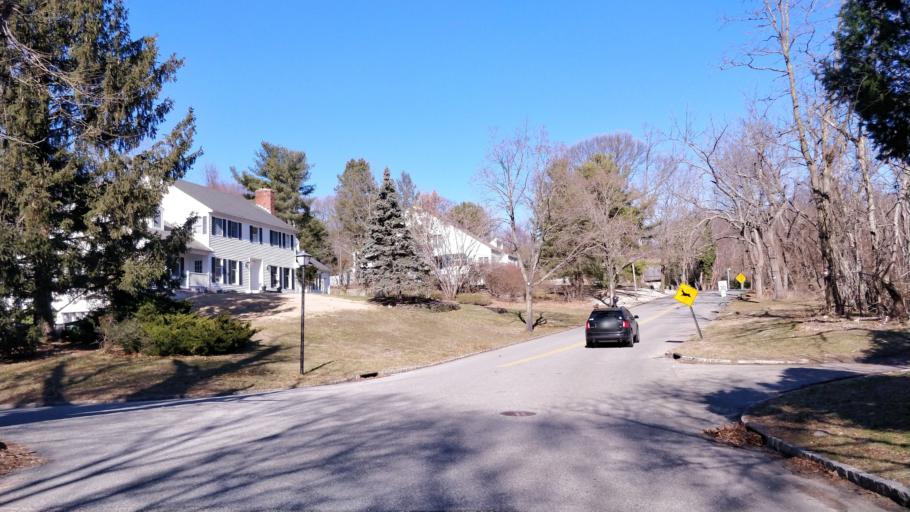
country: US
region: New York
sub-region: Suffolk County
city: Mount Sinai
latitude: 40.9555
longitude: -73.0459
